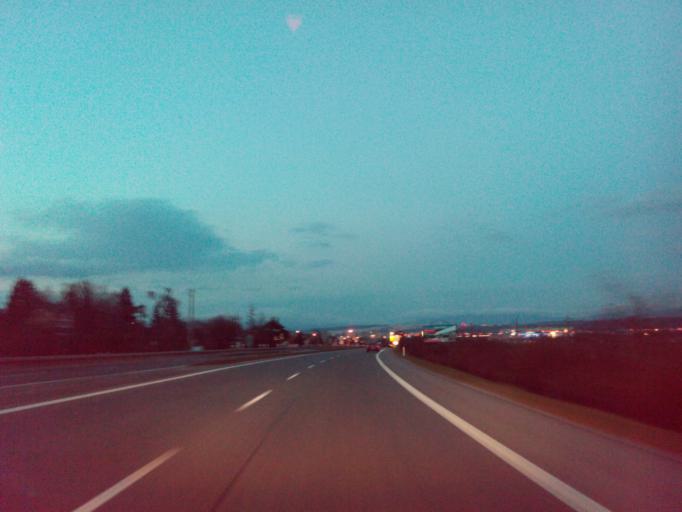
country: SK
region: Kosicky
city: Kosice
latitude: 48.6819
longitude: 21.2152
